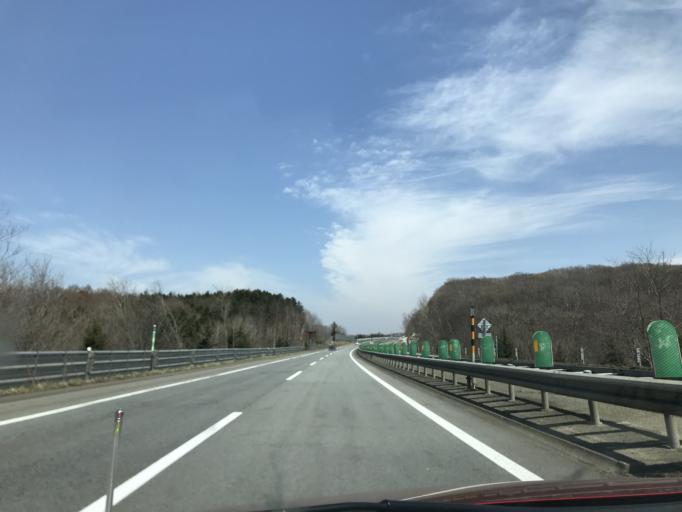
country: JP
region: Hokkaido
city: Bibai
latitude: 43.2581
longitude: 141.8343
